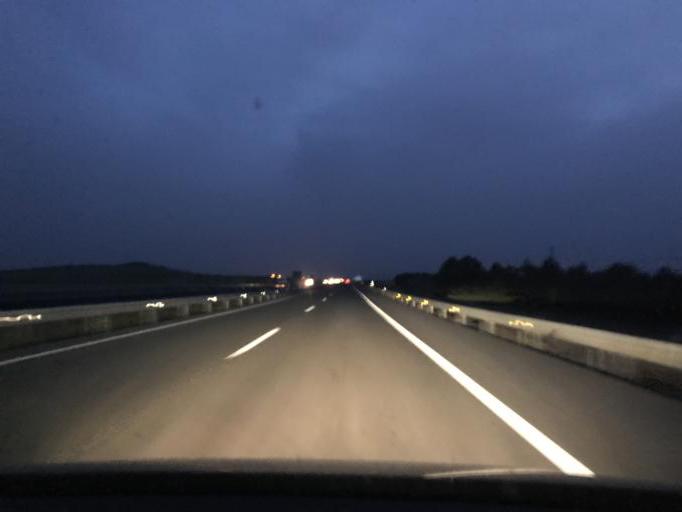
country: ES
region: Andalusia
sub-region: Provincia de Granada
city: Gor
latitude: 37.3857
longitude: -3.0495
